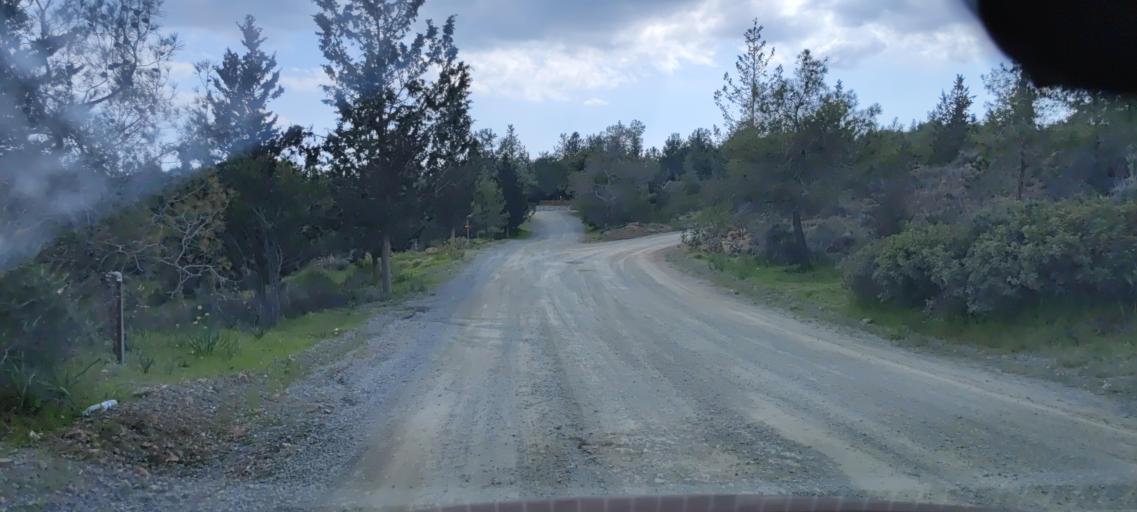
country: CY
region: Larnaka
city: Kornos
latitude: 34.9071
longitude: 33.4013
